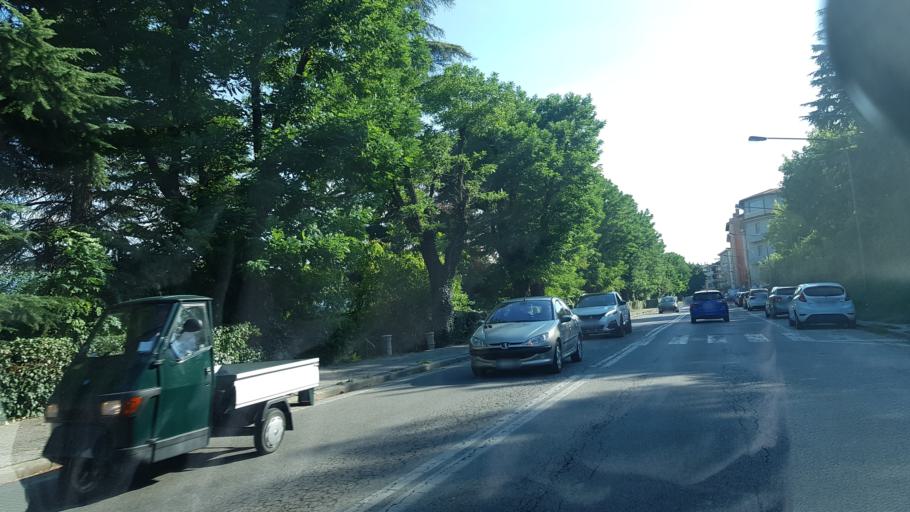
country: IT
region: Piedmont
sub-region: Provincia di Cuneo
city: Cuneo
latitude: 44.3895
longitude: 7.5520
